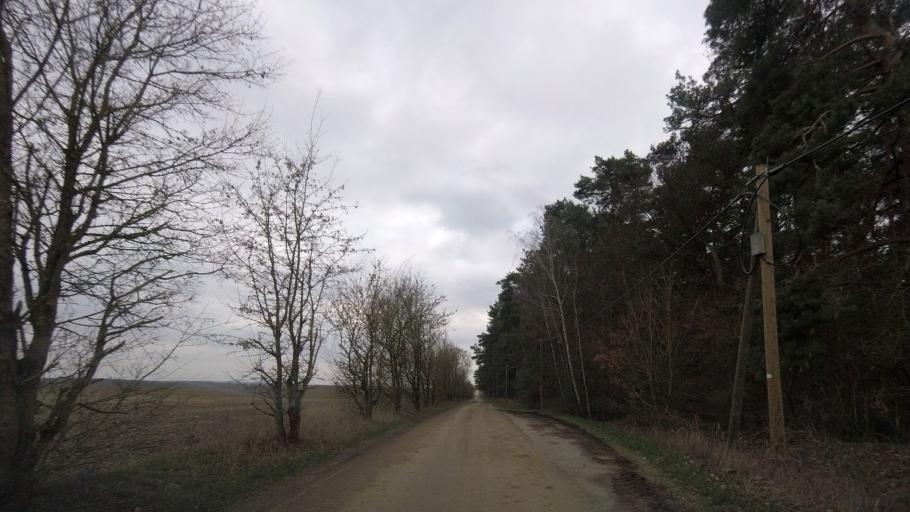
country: DE
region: Saxony-Anhalt
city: Seyda
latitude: 51.9179
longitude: 12.8879
